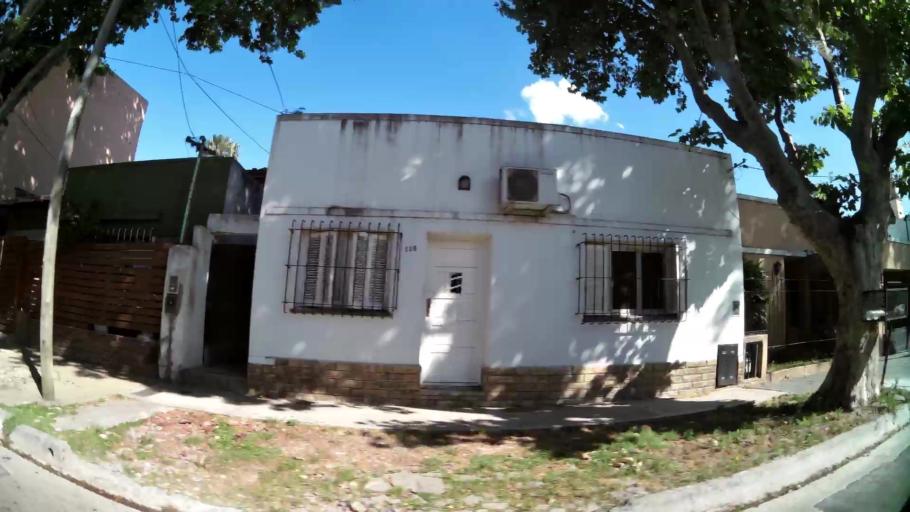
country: AR
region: Buenos Aires
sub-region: Partido de San Isidro
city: San Isidro
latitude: -34.4577
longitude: -58.5351
